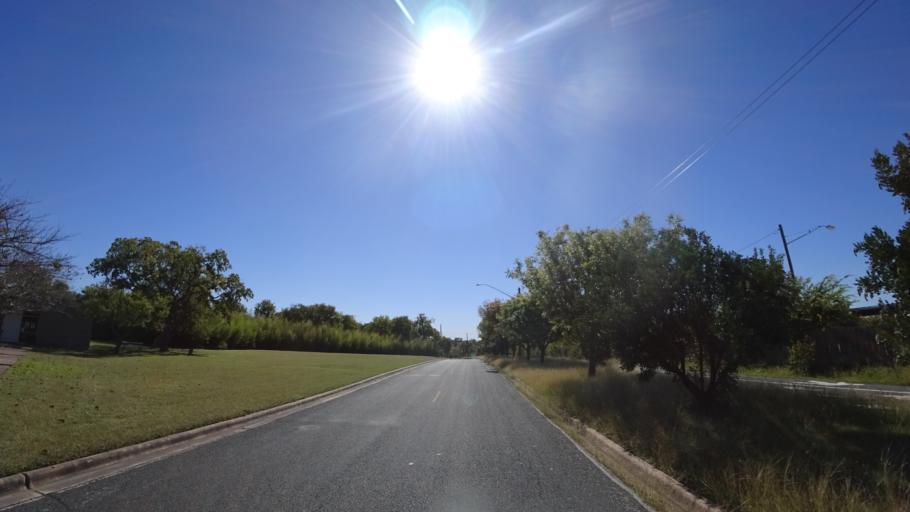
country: US
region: Texas
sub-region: Travis County
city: Austin
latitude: 30.2876
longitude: -97.6988
